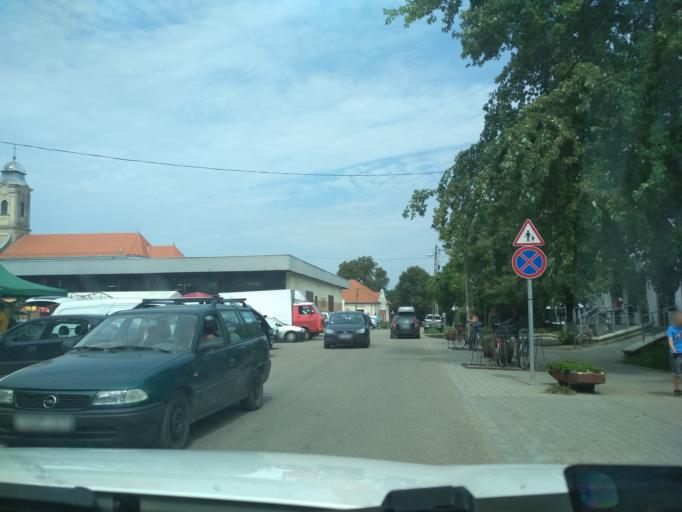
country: HU
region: Jasz-Nagykun-Szolnok
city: Tiszafured
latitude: 47.6165
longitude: 20.7600
